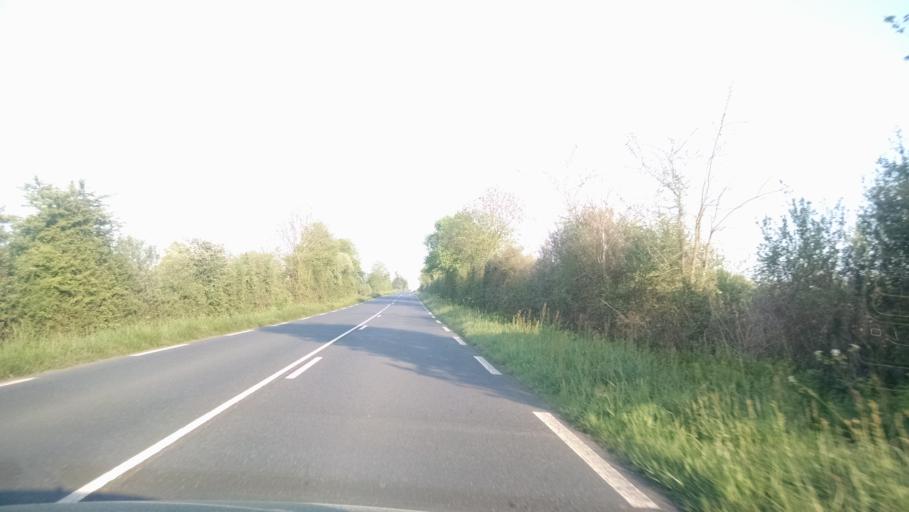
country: FR
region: Pays de la Loire
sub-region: Departement de la Loire-Atlantique
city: Getigne
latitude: 47.0715
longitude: -1.2197
